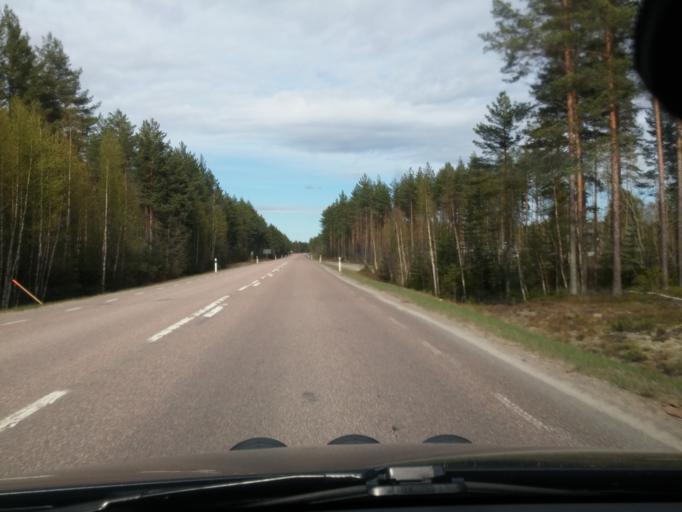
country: SE
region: Gaevleborg
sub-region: Ljusdals Kommun
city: Farila
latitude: 61.8019
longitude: 15.8975
